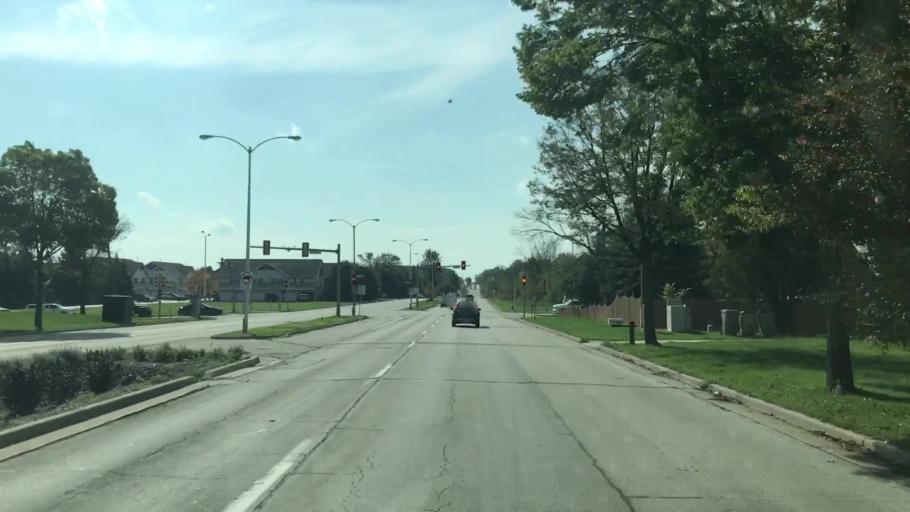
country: US
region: Wisconsin
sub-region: Waukesha County
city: Butler
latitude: 43.1638
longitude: -88.0445
